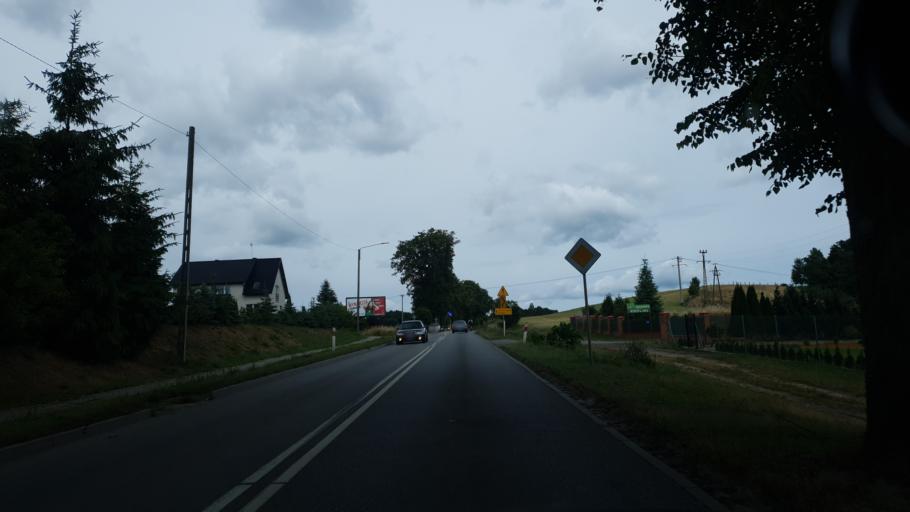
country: PL
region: Pomeranian Voivodeship
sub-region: Powiat kartuski
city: Przodkowo
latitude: 54.3804
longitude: 18.3167
